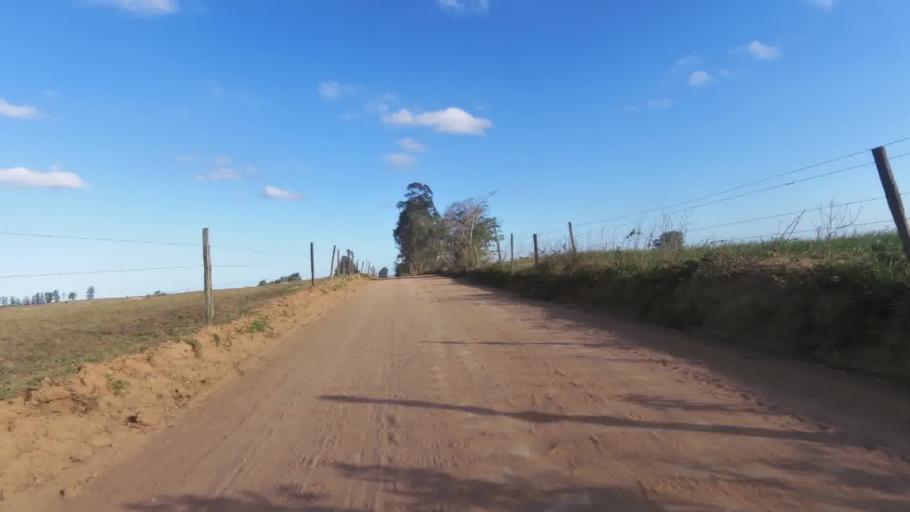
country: BR
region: Espirito Santo
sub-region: Marataizes
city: Marataizes
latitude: -21.1614
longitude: -41.0578
